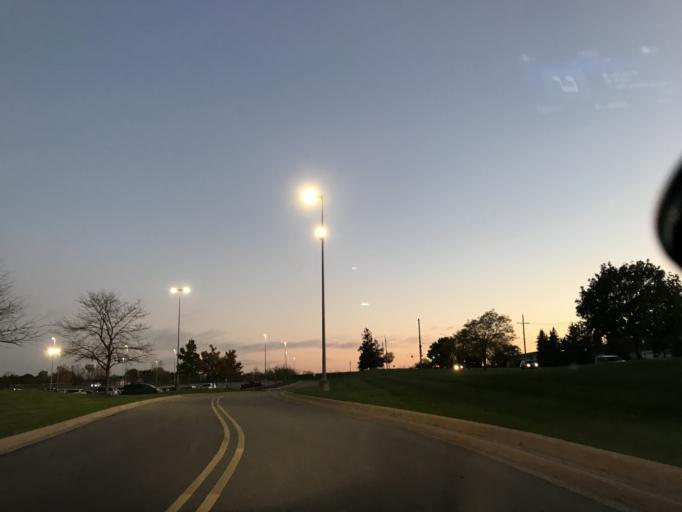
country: US
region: Michigan
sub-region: Oakland County
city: South Lyon
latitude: 42.4733
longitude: -83.6518
